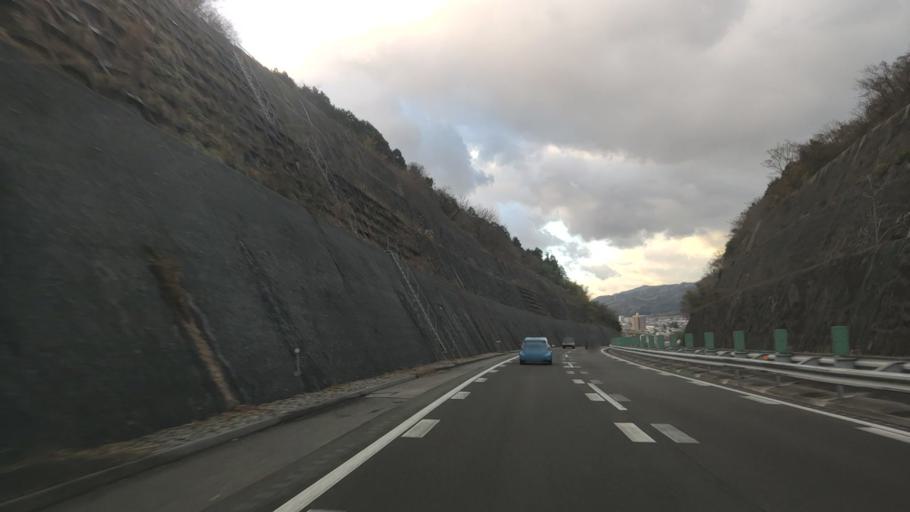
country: JP
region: Ehime
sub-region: Shikoku-chuo Shi
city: Matsuyama
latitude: 33.7910
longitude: 132.9155
